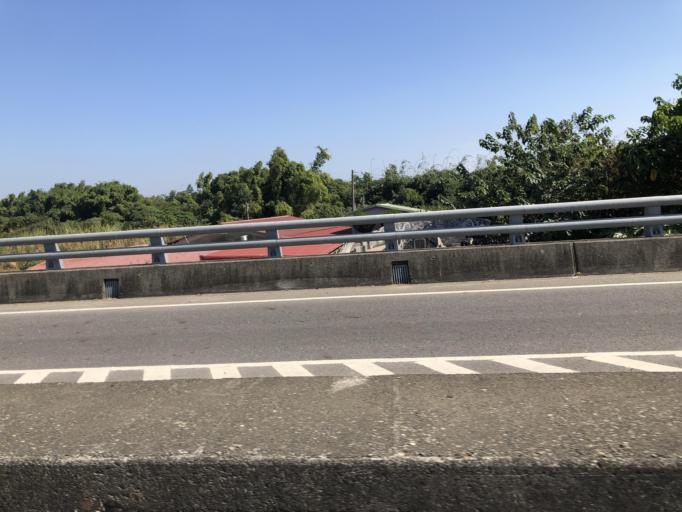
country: TW
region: Taiwan
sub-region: Tainan
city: Tainan
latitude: 23.0332
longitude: 120.3222
